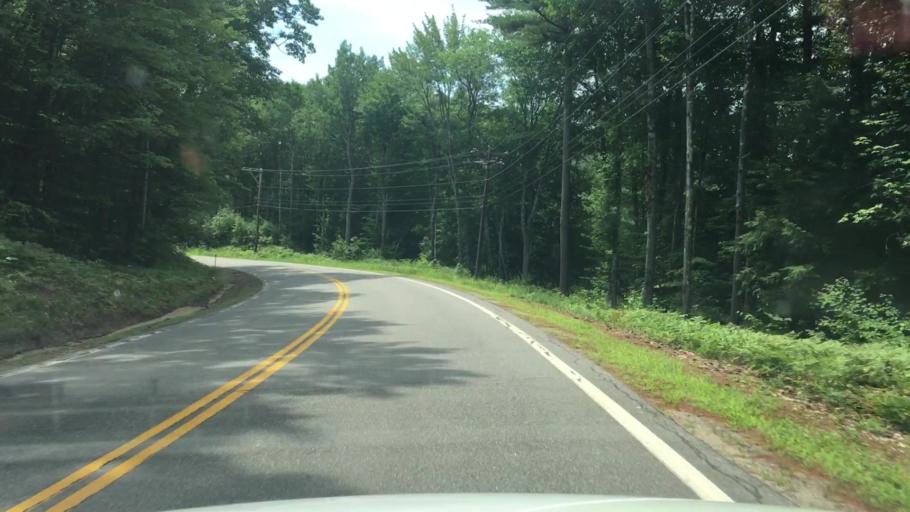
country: US
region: New Hampshire
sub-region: Grafton County
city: Plymouth
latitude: 43.7647
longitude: -71.6747
